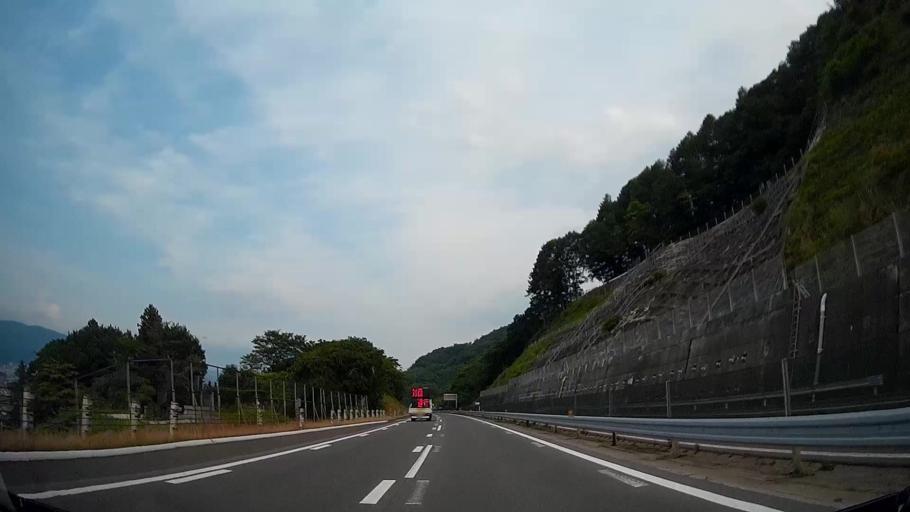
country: JP
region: Nagano
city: Suwa
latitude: 36.0064
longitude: 138.0962
